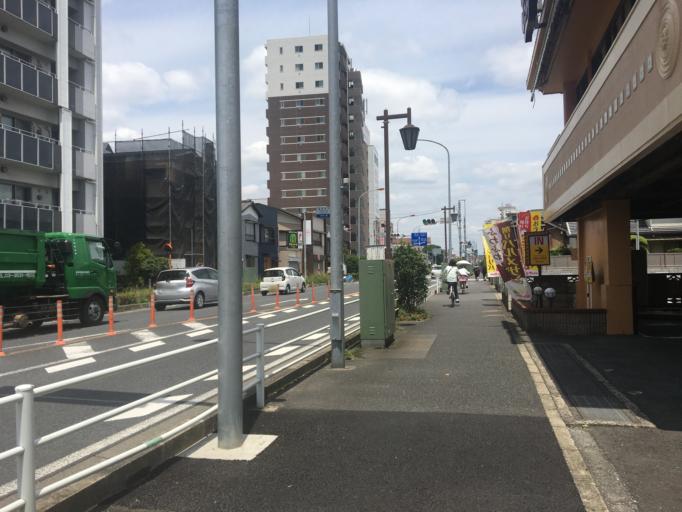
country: JP
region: Saitama
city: Shimotoda
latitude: 35.8148
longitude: 139.6822
